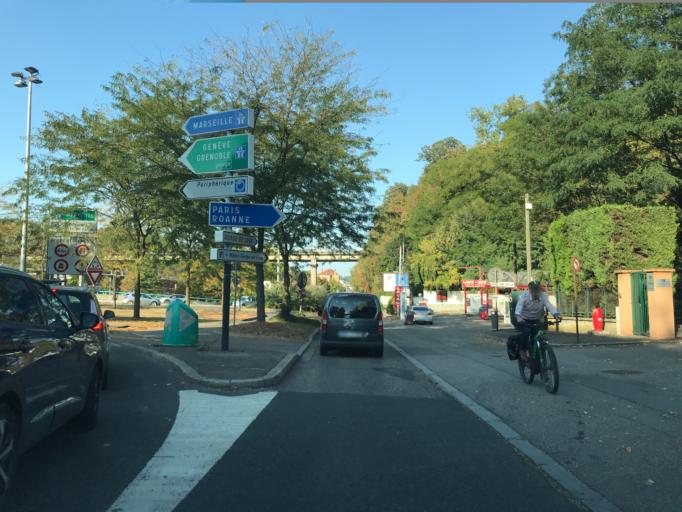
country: FR
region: Rhone-Alpes
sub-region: Departement du Rhone
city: Tassin-la-Demi-Lune
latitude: 45.7696
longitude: 4.7881
